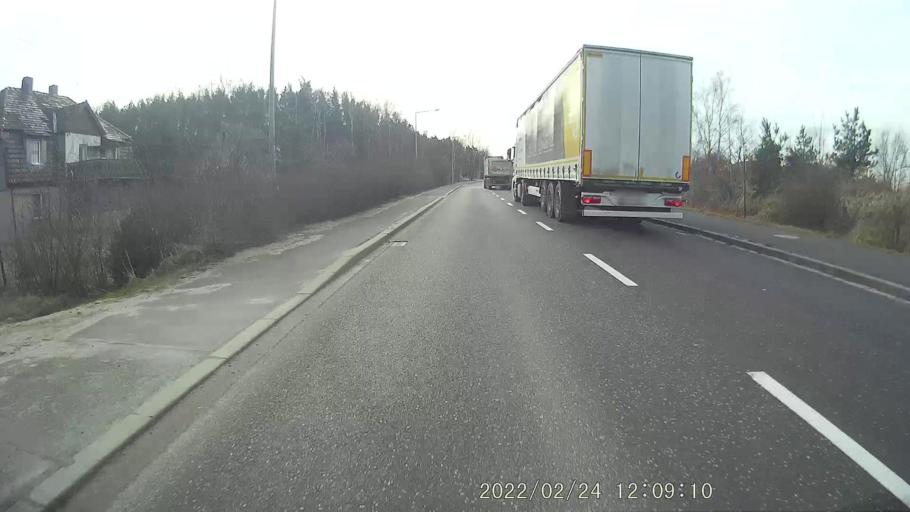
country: PL
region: Lower Silesian Voivodeship
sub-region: Powiat glogowski
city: Glogow
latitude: 51.6483
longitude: 16.0763
